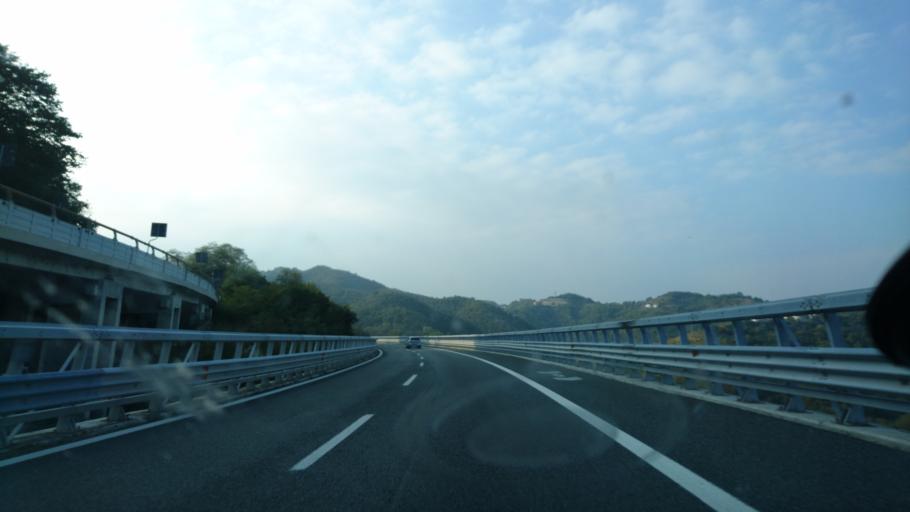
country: IT
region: Liguria
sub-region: Provincia di Savona
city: Altare
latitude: 44.3236
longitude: 8.3755
